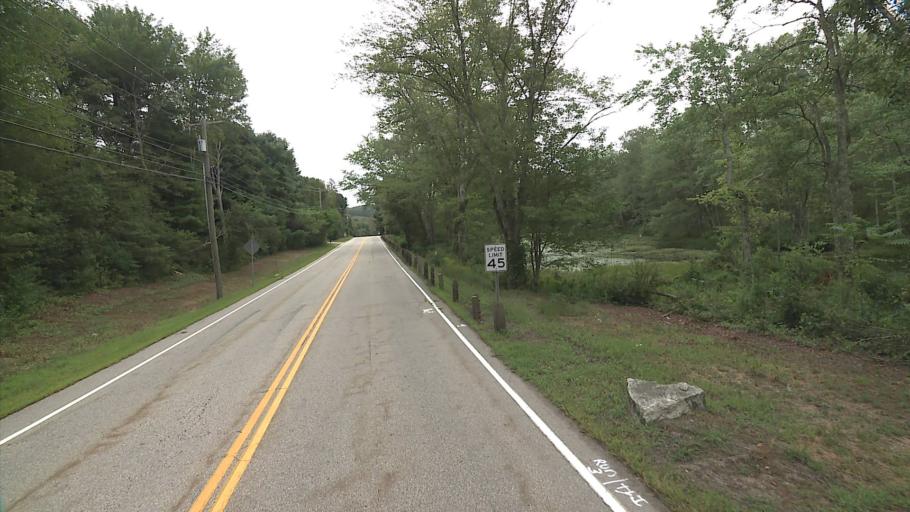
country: US
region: Connecticut
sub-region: Middlesex County
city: Essex Village
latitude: 41.4344
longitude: -72.3393
